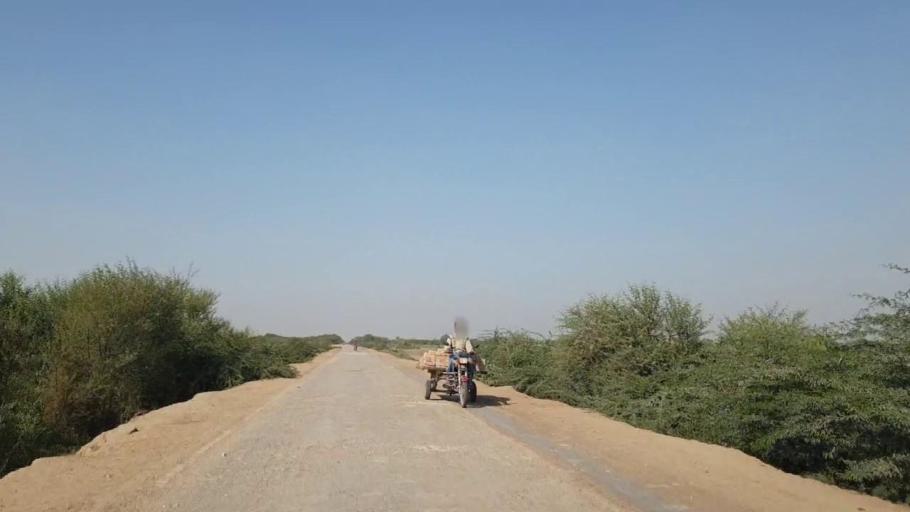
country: PK
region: Sindh
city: Digri
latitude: 24.9875
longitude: 69.1094
